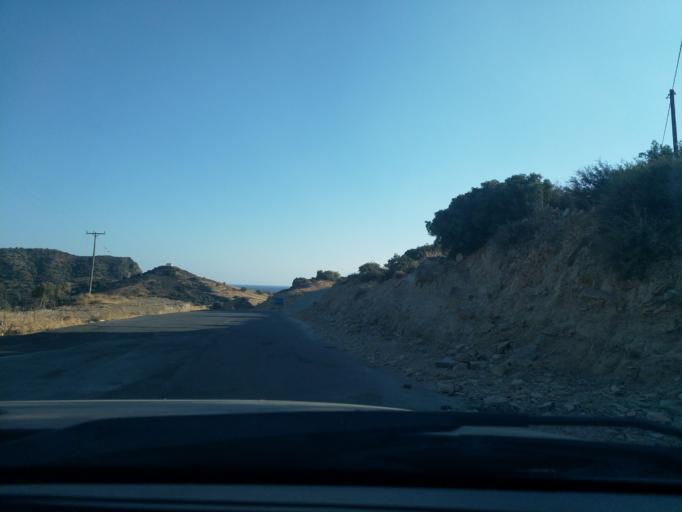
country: GR
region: Crete
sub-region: Nomos Rethymnis
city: Agia Galini
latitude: 35.1211
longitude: 24.5585
